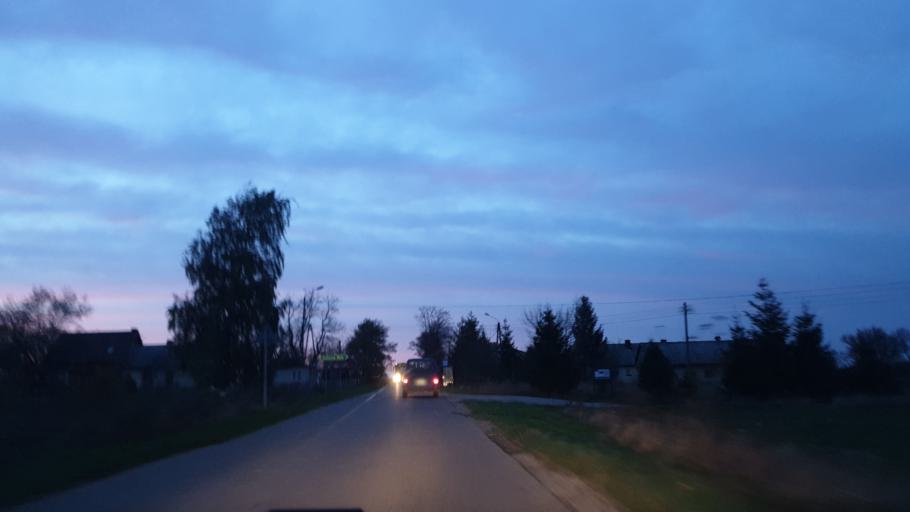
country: PL
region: Pomeranian Voivodeship
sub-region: Powiat pucki
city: Krokowa
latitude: 54.7765
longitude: 18.2080
